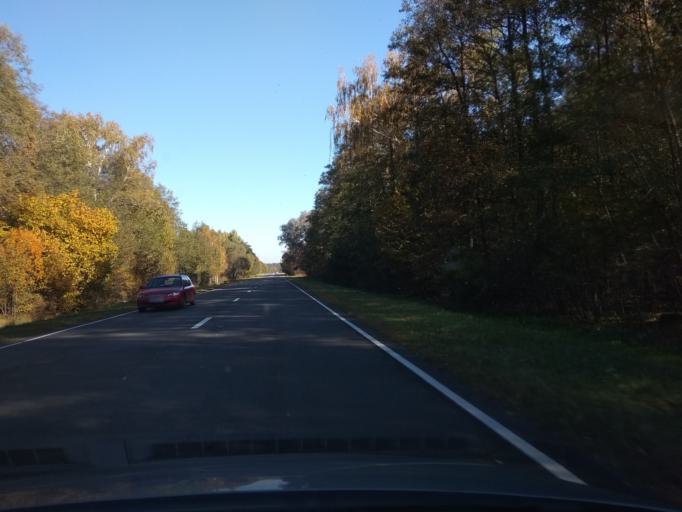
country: BY
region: Brest
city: Kobryn
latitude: 52.0177
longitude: 24.2386
